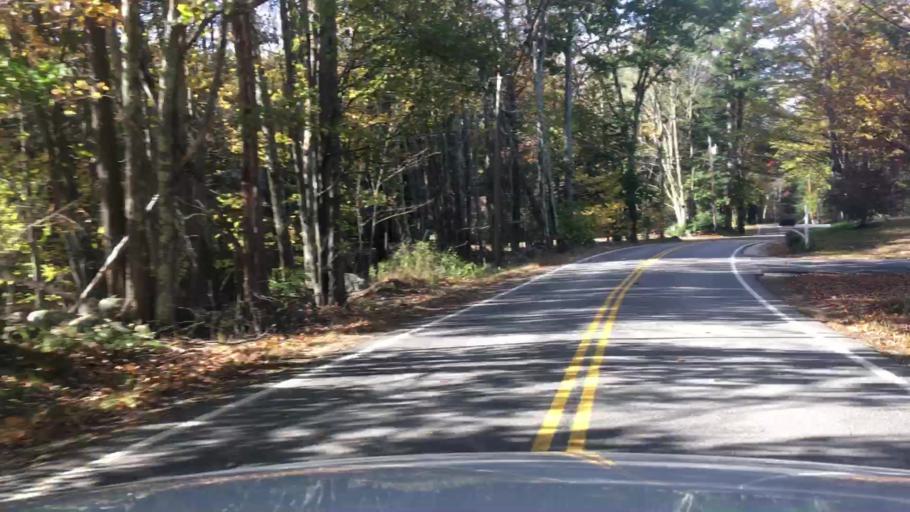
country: US
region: New Hampshire
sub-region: Strafford County
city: Barrington
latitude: 43.1802
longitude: -71.0359
